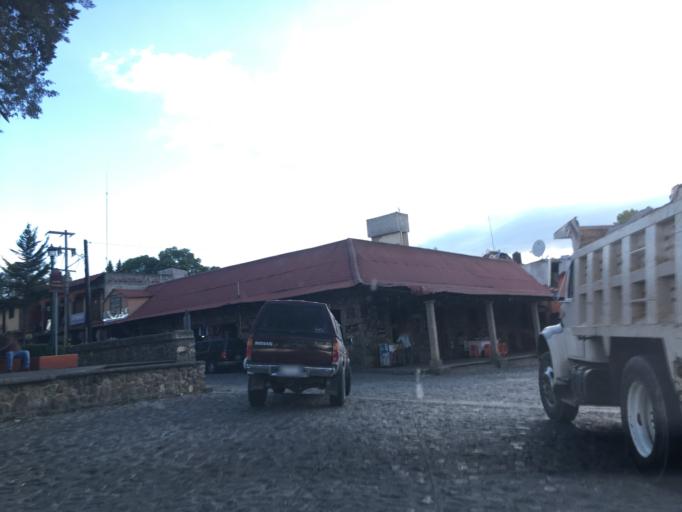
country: MX
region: Hidalgo
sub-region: Omitlan de Juarez
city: San Antonio el Paso
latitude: 20.2035
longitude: -98.5767
